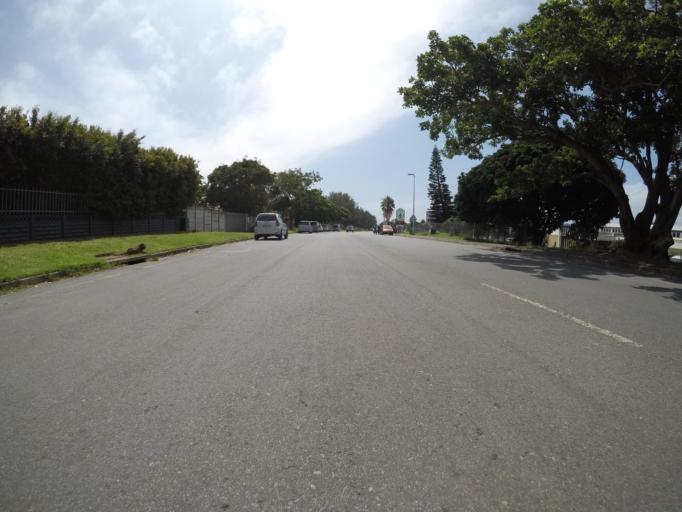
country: ZA
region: Eastern Cape
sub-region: Buffalo City Metropolitan Municipality
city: East London
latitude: -32.9403
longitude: 28.0224
